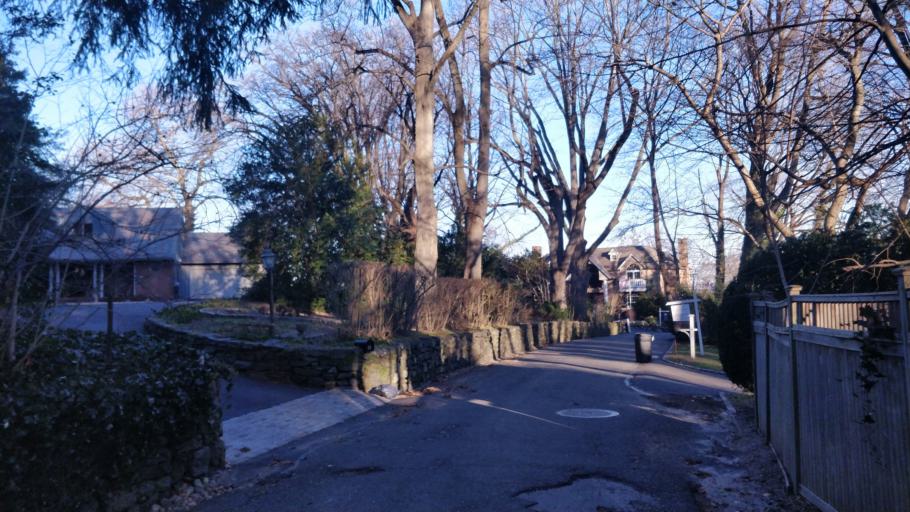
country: US
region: New York
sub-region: Nassau County
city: Glen Cove
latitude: 40.8790
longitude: -73.6486
